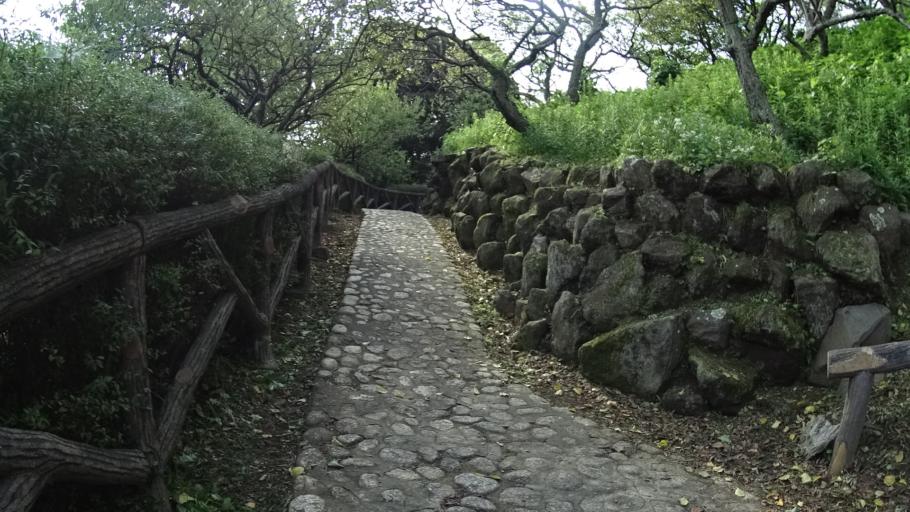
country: JP
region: Kanagawa
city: Yokosuka
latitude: 35.2863
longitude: 139.6323
